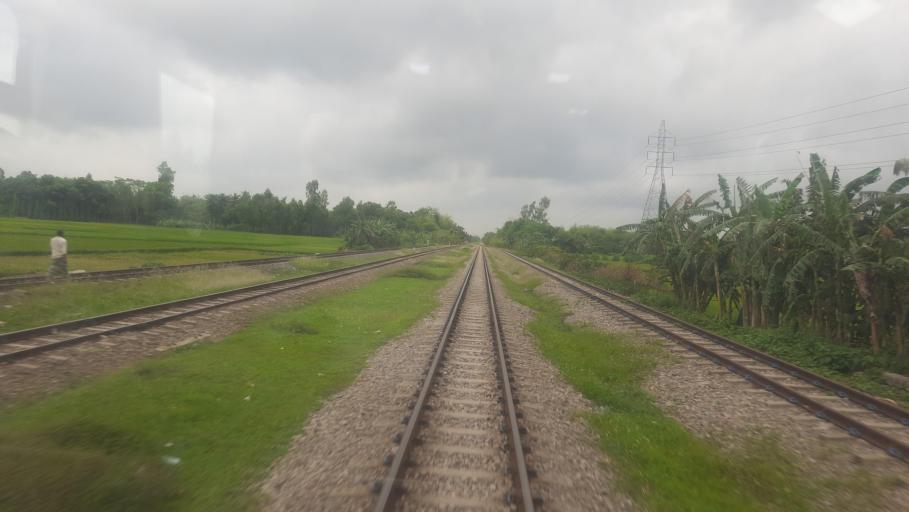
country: BD
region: Dhaka
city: Bhairab Bazar
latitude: 24.0051
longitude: 90.9004
